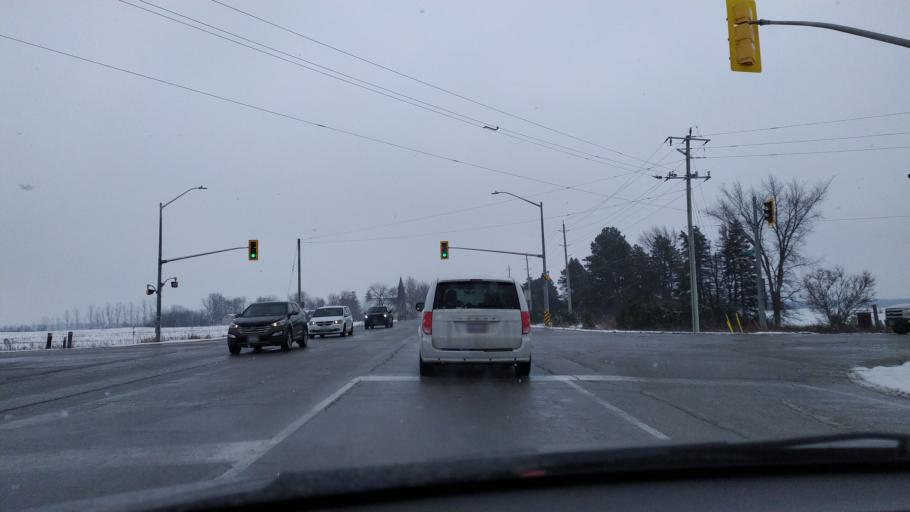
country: CA
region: Ontario
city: Waterloo
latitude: 43.6240
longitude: -80.6954
